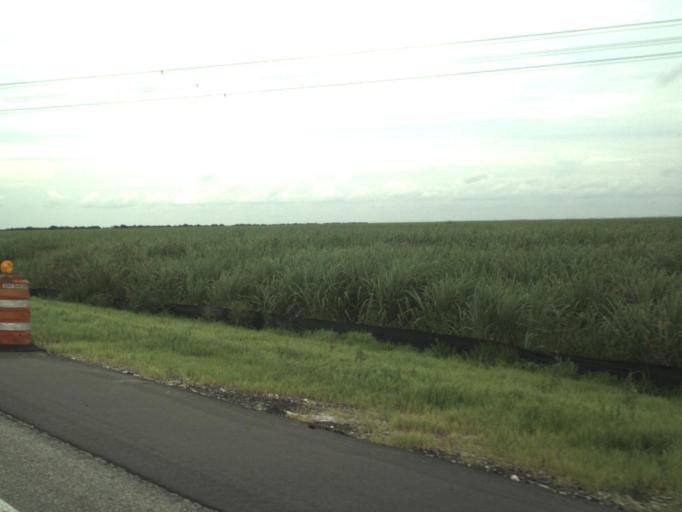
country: US
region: Florida
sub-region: Palm Beach County
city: Loxahatchee Groves
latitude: 26.7095
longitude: -80.4183
